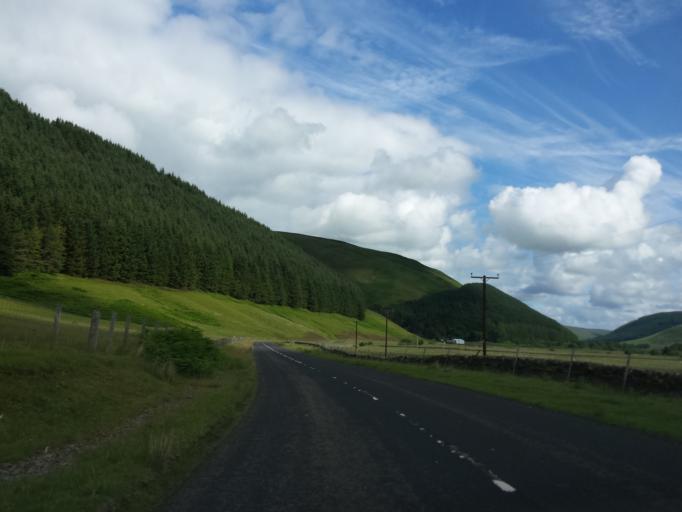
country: GB
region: Scotland
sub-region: The Scottish Borders
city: Peebles
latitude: 55.4510
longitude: -3.2213
